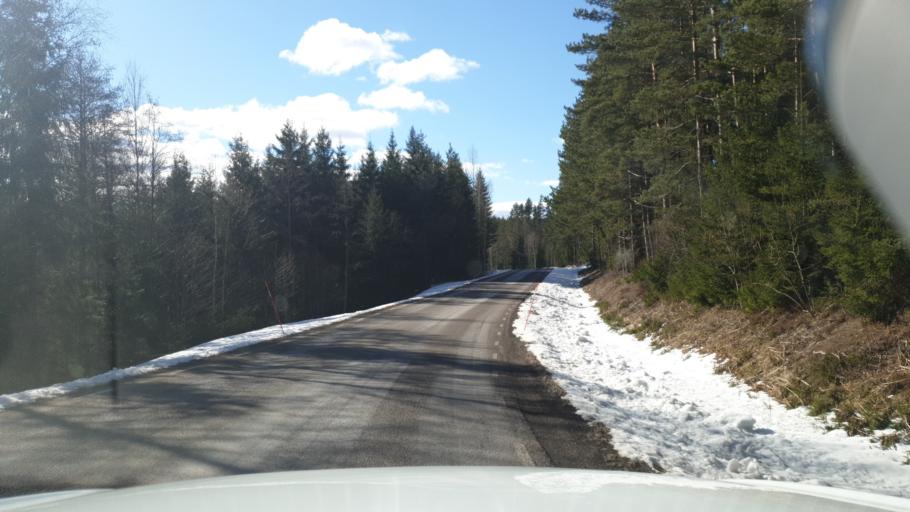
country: SE
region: Vaermland
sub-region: Arvika Kommun
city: Arvika
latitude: 59.6124
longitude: 12.7816
